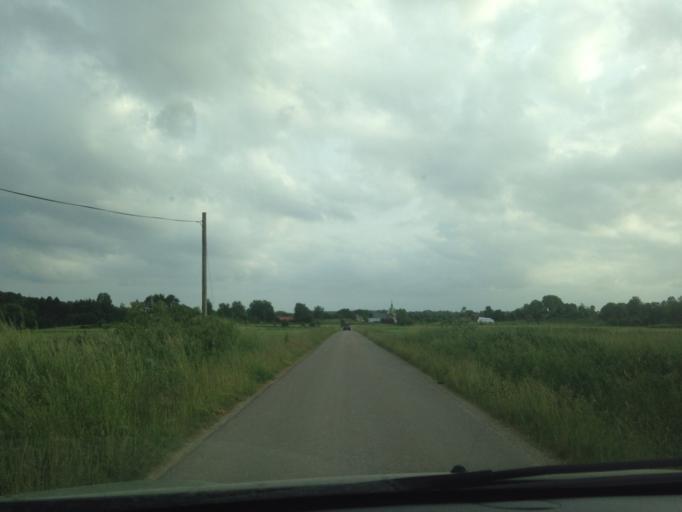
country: SE
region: Vaestra Goetaland
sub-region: Kungalvs Kommun
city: Kungalv
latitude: 57.8074
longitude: 11.9238
